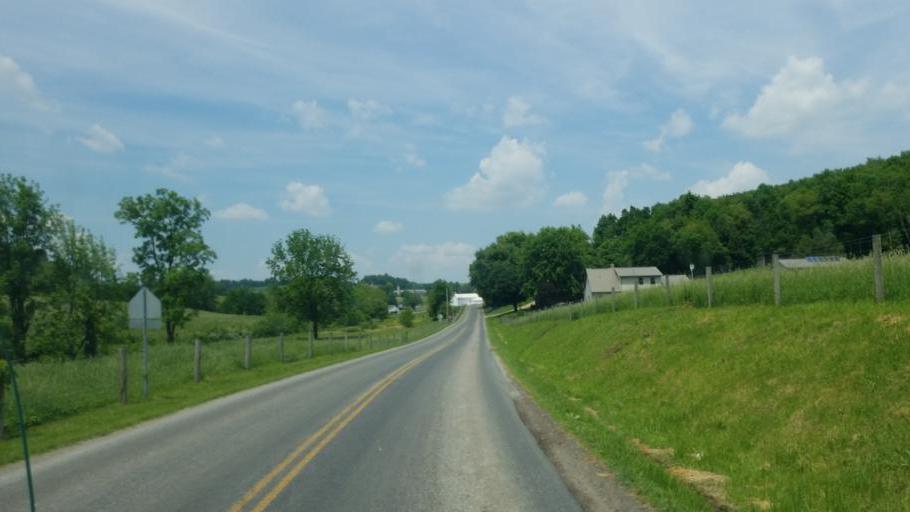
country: US
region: Ohio
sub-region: Tuscarawas County
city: Sugarcreek
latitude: 40.4982
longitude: -81.7832
